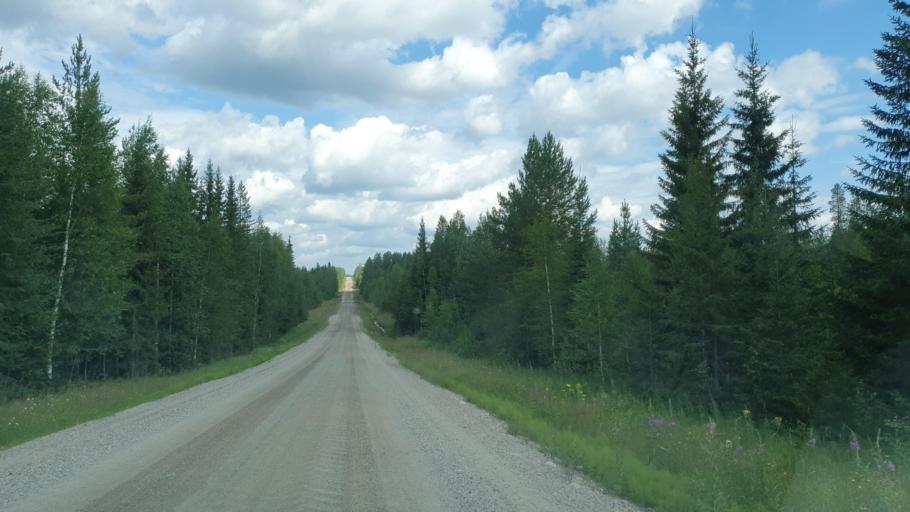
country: FI
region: Kainuu
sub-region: Kehys-Kainuu
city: Kuhmo
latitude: 64.4672
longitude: 29.5984
